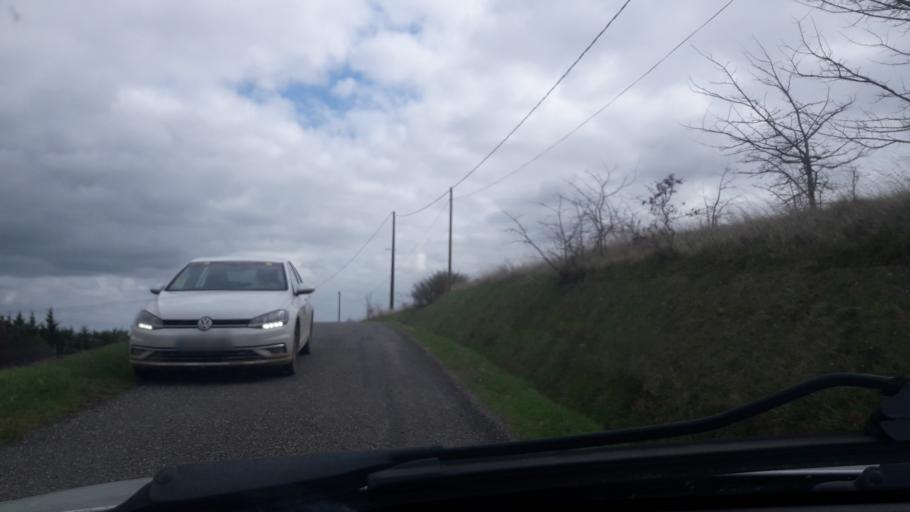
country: FR
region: Midi-Pyrenees
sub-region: Departement de l'Ariege
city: Lezat-sur-Leze
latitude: 43.1972
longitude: 1.3194
